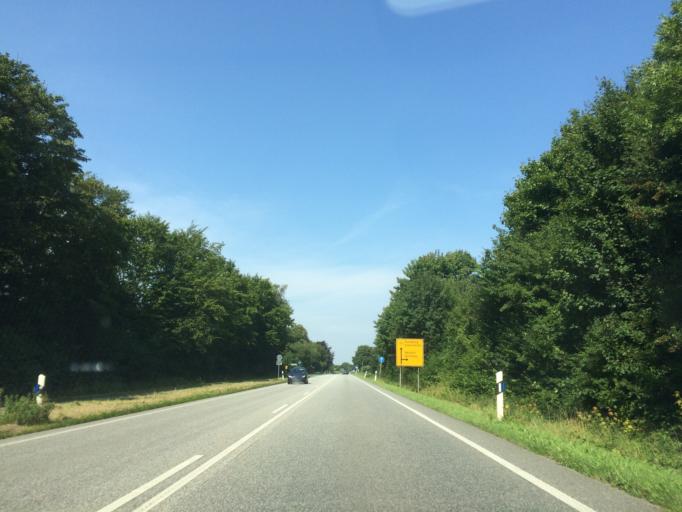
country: DE
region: Schleswig-Holstein
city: Neudorf-Bornstein
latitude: 54.4310
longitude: 9.9462
